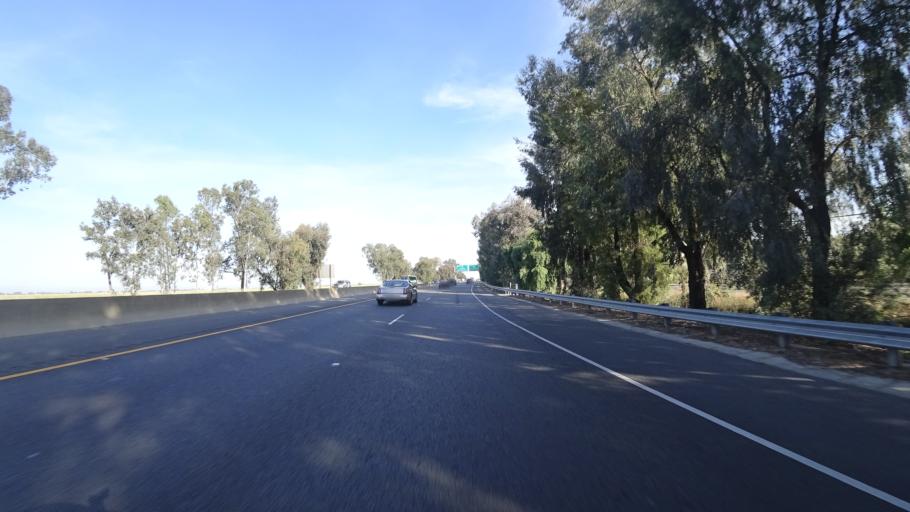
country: US
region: California
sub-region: Yuba County
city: Olivehurst
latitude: 39.1002
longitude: -121.5472
